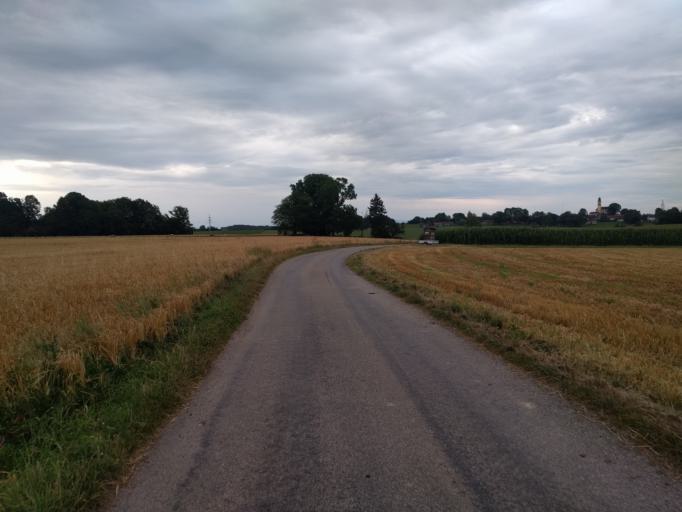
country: DE
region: Bavaria
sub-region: Upper Bavaria
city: Schaftlarn
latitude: 48.0009
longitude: 11.4473
